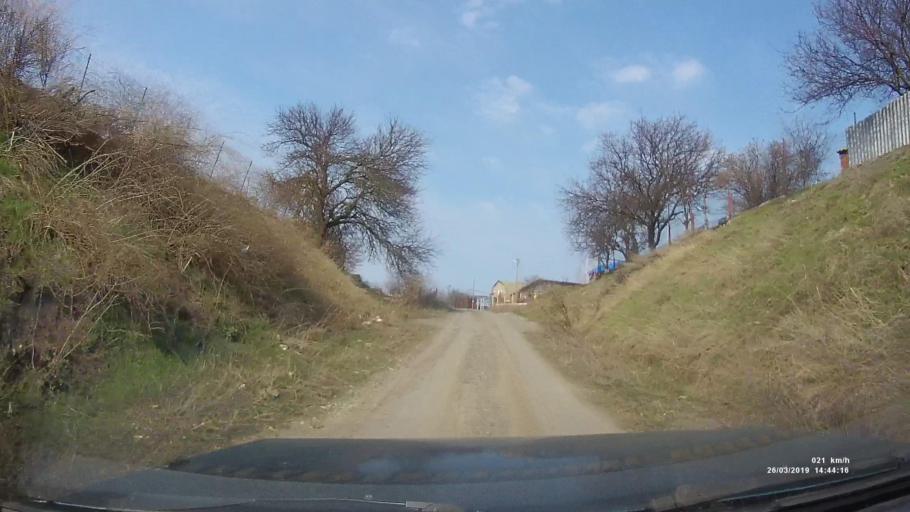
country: RU
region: Rostov
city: Novobessergenovka
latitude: 47.1771
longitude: 38.8624
